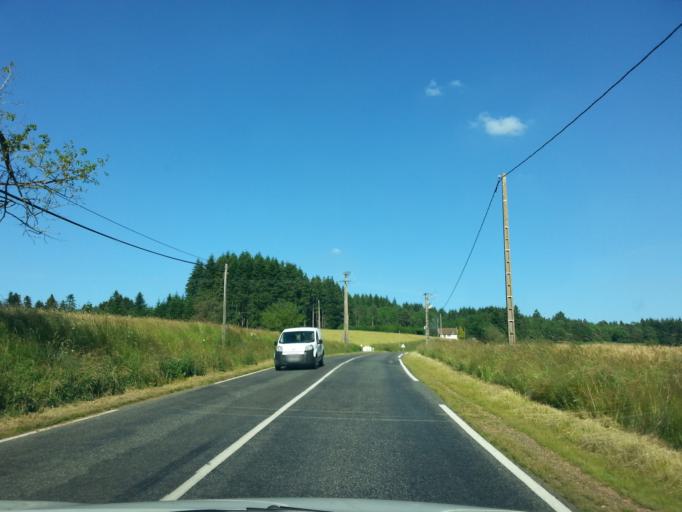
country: FR
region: Rhone-Alpes
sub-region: Departement de la Loire
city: Belmont-de-la-Loire
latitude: 46.1792
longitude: 4.4131
